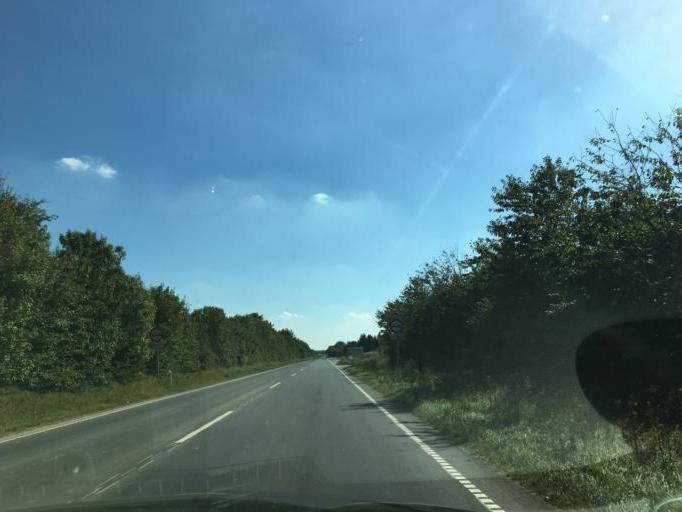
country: DK
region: South Denmark
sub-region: Kolding Kommune
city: Lunderskov
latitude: 55.4984
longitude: 9.2901
